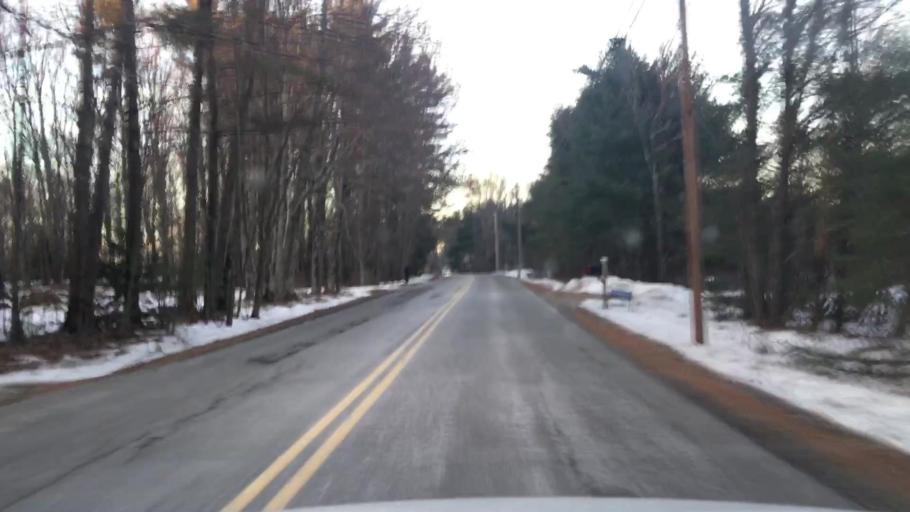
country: US
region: Maine
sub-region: York County
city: Lebanon
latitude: 43.3355
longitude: -70.8636
